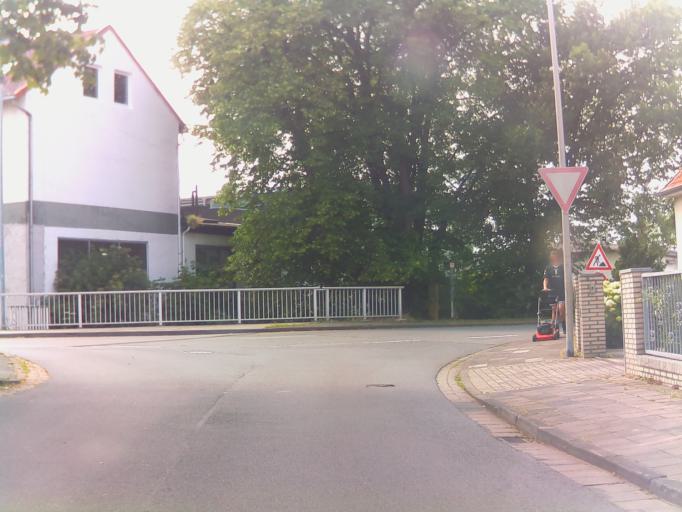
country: DE
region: Lower Saxony
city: Hildesheim
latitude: 52.1720
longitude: 9.9897
